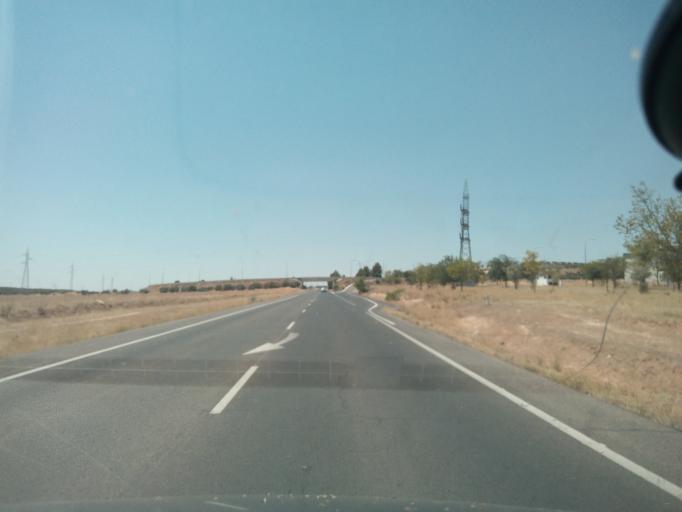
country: ES
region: Castille-La Mancha
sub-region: Province of Toledo
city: Villacanas
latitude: 39.6102
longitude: -3.3522
